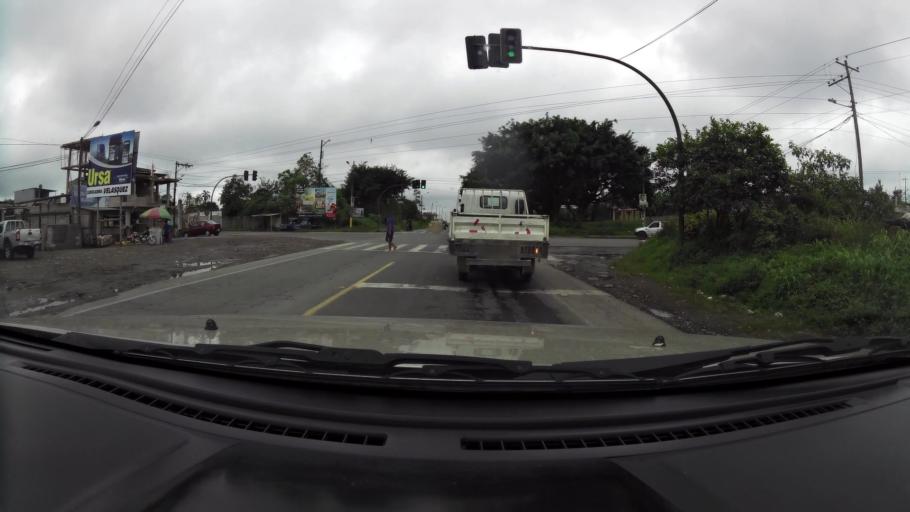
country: EC
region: Santo Domingo de los Tsachilas
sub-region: Canton Santo Domingo de los Colorados
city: Santo Domingo de los Colorados
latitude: -0.2818
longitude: -79.1834
